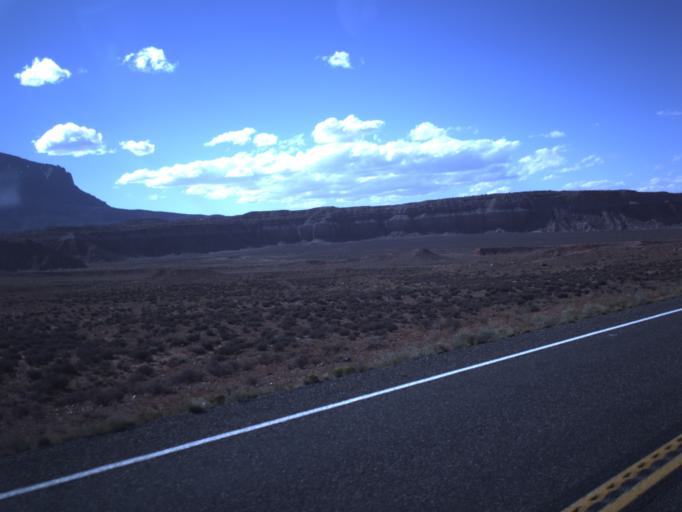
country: US
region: Utah
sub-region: Wayne County
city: Loa
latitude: 38.1489
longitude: -110.6187
